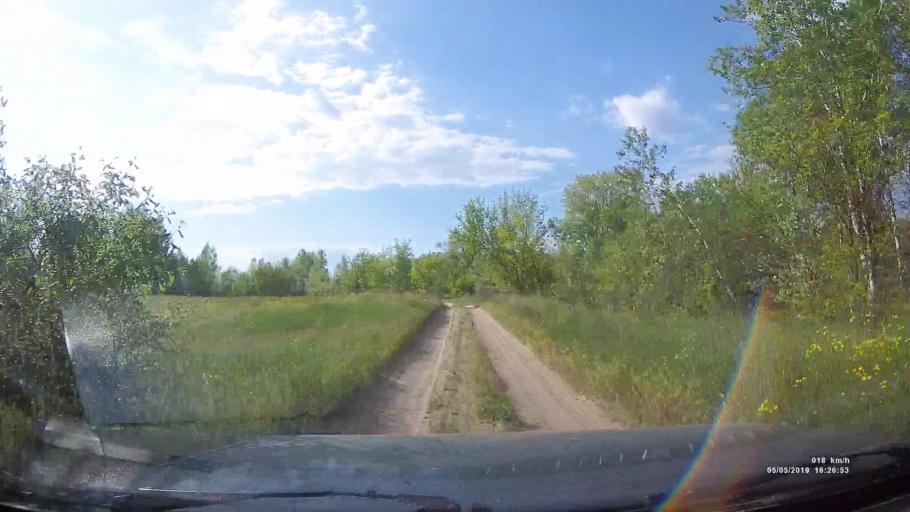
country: RU
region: Rostov
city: Ust'-Donetskiy
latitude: 47.7639
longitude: 41.0206
